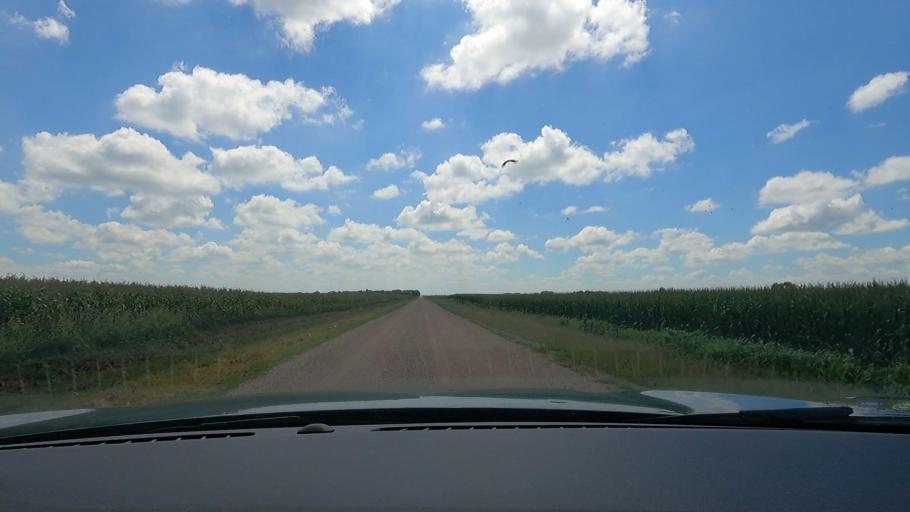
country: US
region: Nebraska
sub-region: Saunders County
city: Wahoo
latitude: 41.2758
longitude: -96.5419
